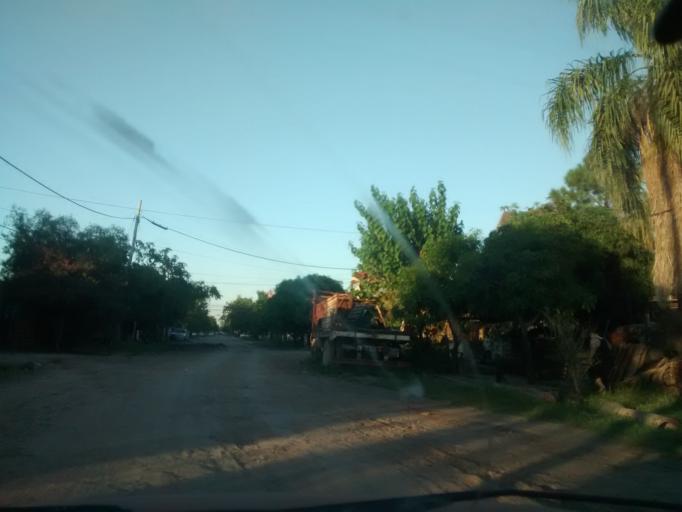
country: AR
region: Chaco
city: Resistencia
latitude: -27.4603
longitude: -59.0001
